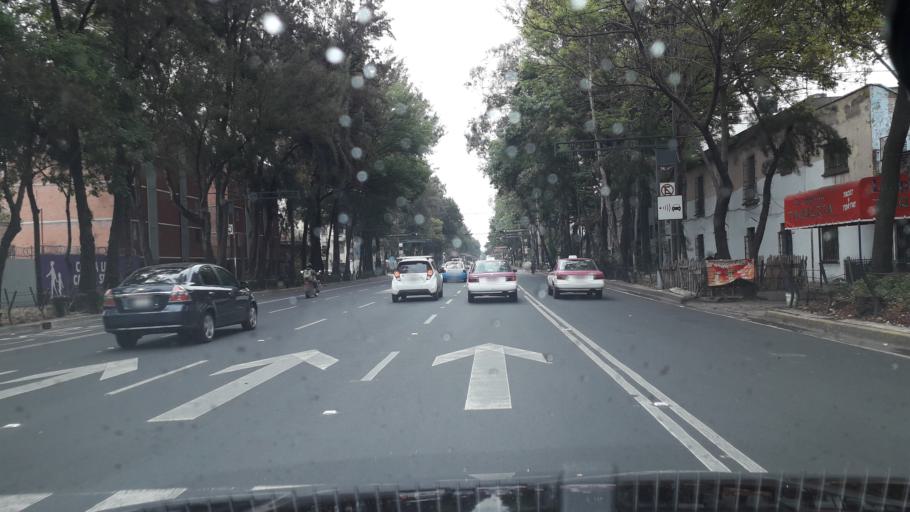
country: MX
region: Mexico City
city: Cuauhtemoc
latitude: 19.4477
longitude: -99.1615
